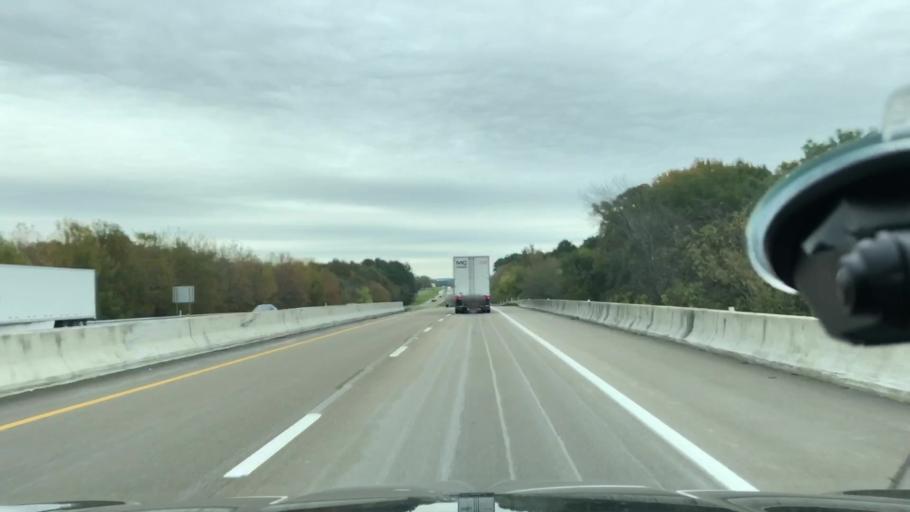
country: US
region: Texas
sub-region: Titus County
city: Mount Pleasant
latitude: 33.1590
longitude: -95.0339
